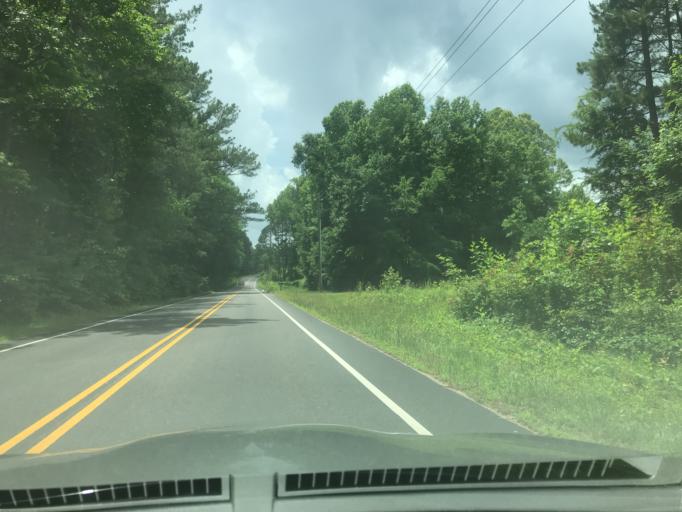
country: US
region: North Carolina
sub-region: Wake County
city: Knightdale
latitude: 35.8363
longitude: -78.4852
